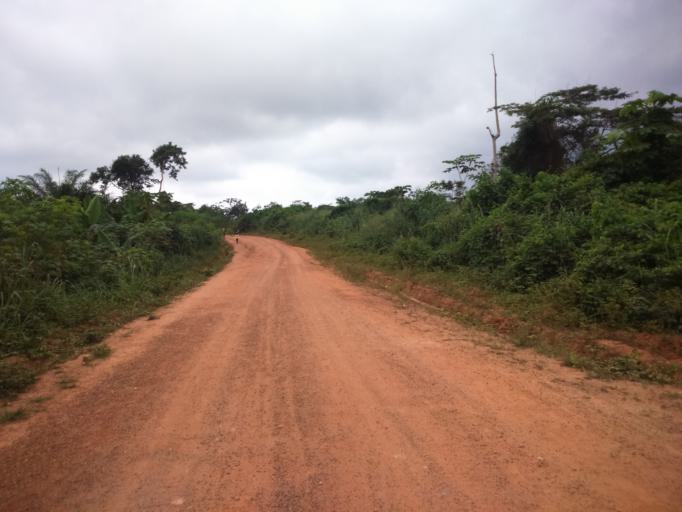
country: CI
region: Lagunes
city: Agou
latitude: 6.0770
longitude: -4.0678
